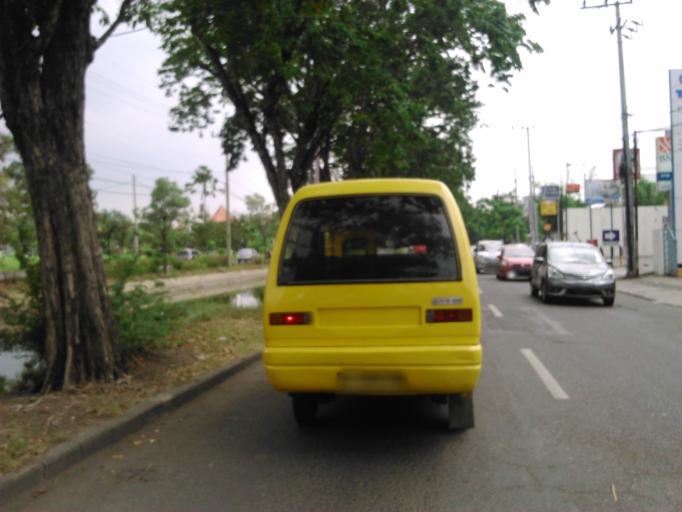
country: ID
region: East Java
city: Semampir
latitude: -7.2903
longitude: 112.7881
